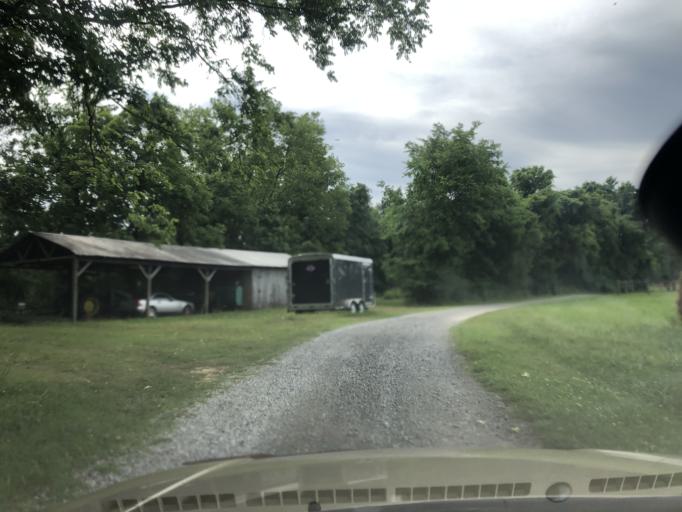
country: US
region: Tennessee
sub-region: Davidson County
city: Lakewood
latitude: 36.2115
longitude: -86.6409
